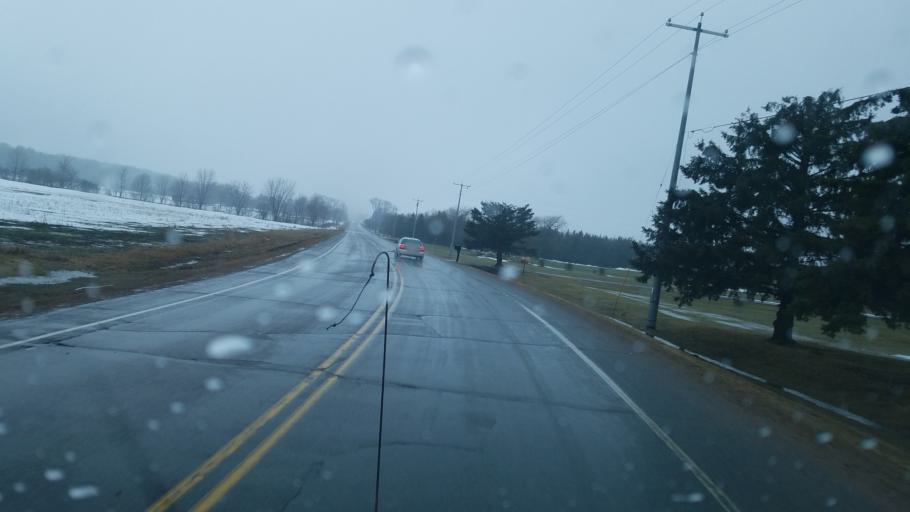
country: US
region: Wisconsin
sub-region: Wood County
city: Marshfield
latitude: 44.6774
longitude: -90.2202
